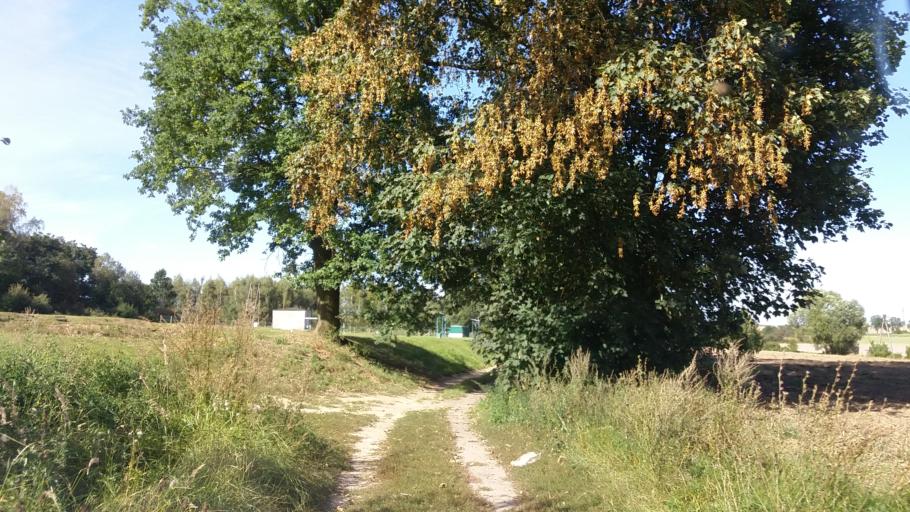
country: PL
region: West Pomeranian Voivodeship
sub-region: Powiat choszczenski
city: Krzecin
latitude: 53.1347
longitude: 15.5038
